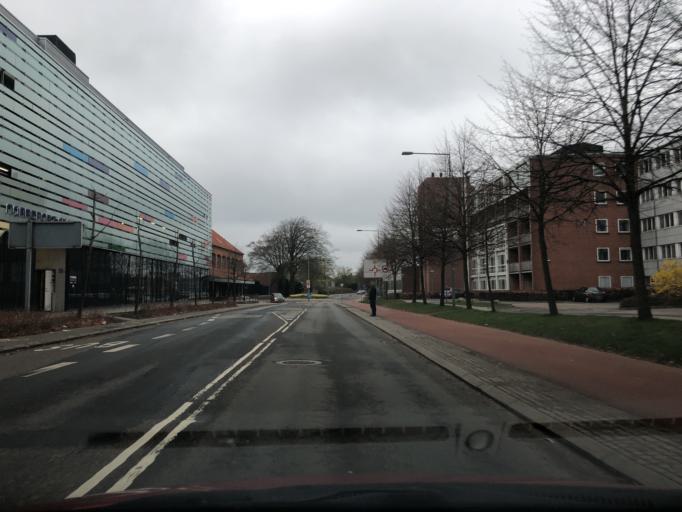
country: DK
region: Central Jutland
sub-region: Holstebro Kommune
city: Holstebro
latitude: 56.3615
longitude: 8.6220
